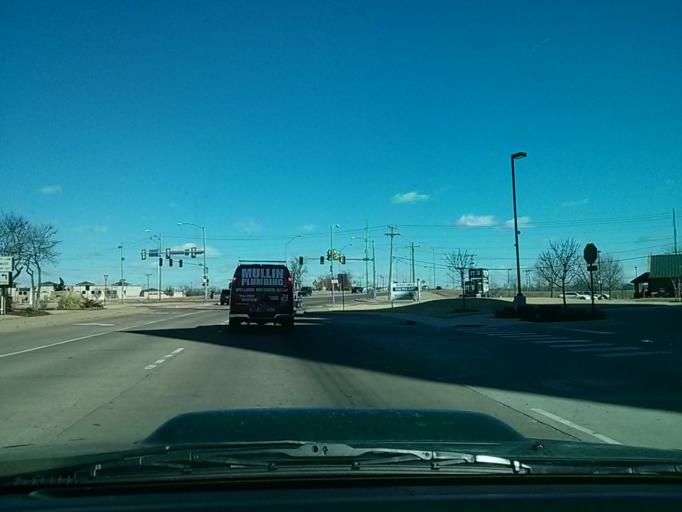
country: US
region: Oklahoma
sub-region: Tulsa County
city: Jenks
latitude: 36.0232
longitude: -95.9610
